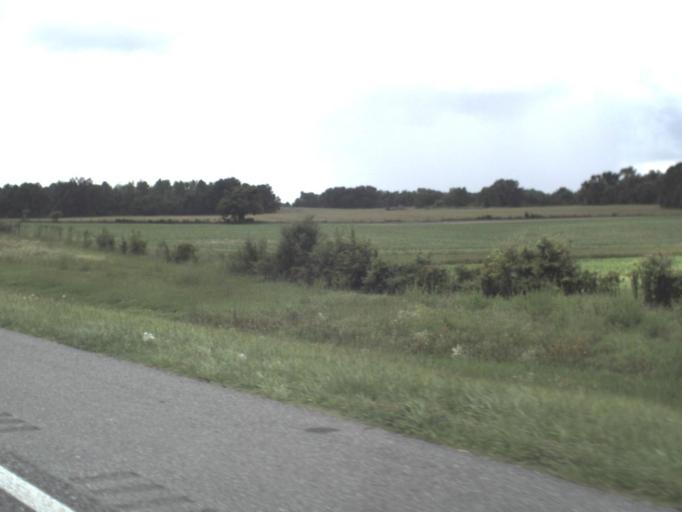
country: US
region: Florida
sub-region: Columbia County
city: Lake City
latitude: 30.0855
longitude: -82.6375
